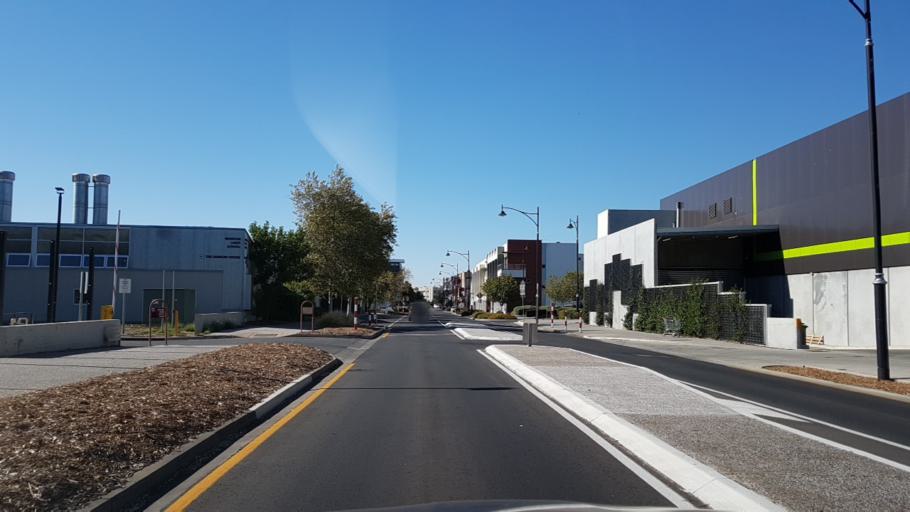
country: AU
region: South Australia
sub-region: Salisbury
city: Ingle Farm
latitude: -34.8099
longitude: 138.6149
